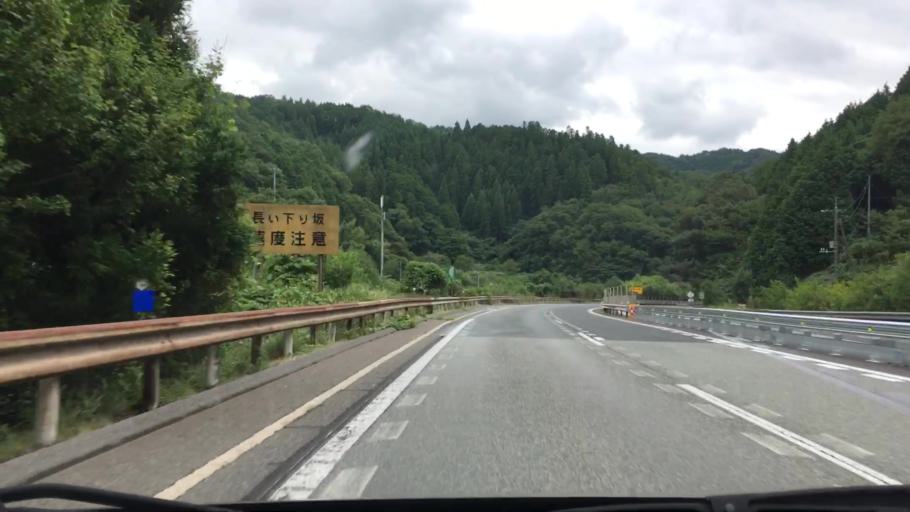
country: JP
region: Okayama
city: Niimi
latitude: 35.0207
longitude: 133.5242
